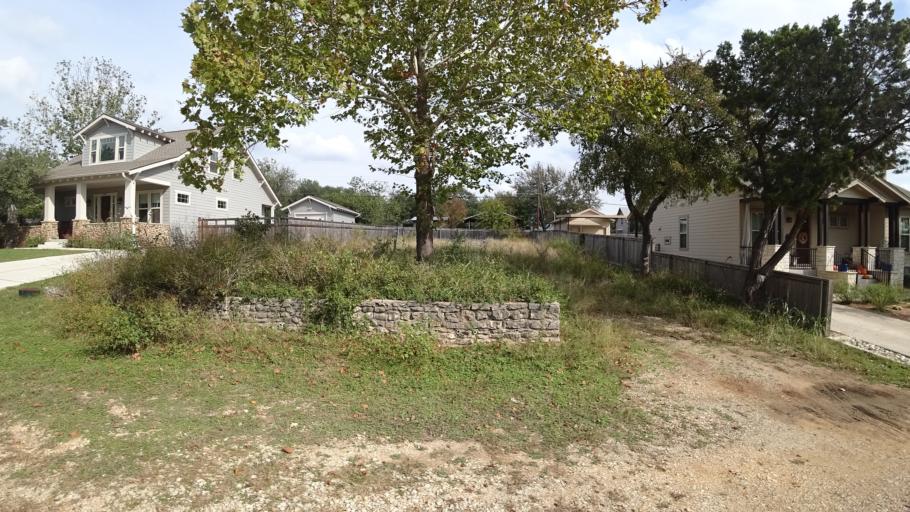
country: US
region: Texas
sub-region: Travis County
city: Hudson Bend
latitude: 30.3814
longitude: -97.9177
